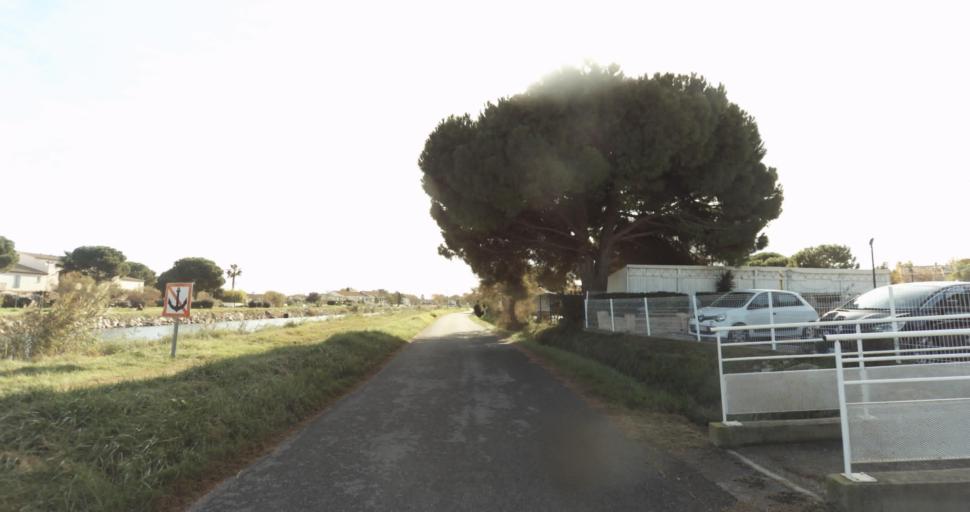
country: FR
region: Languedoc-Roussillon
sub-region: Departement du Gard
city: Aigues-Mortes
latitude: 43.5736
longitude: 4.1852
